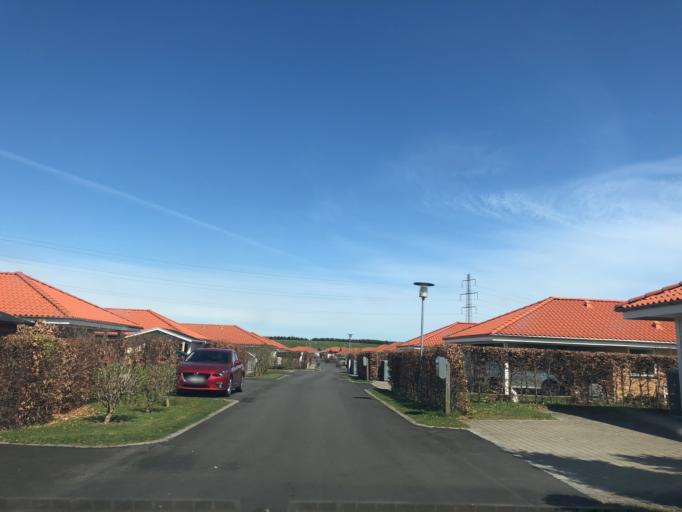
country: DK
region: Zealand
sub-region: Ringsted Kommune
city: Ringsted
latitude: 55.4531
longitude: 11.7696
